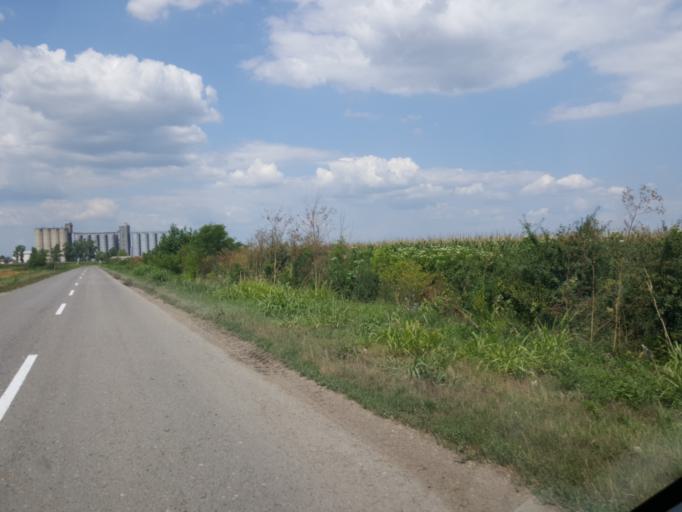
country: RS
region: Autonomna Pokrajina Vojvodina
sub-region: Sremski Okrug
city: Pecinci
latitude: 44.8784
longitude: 19.9612
